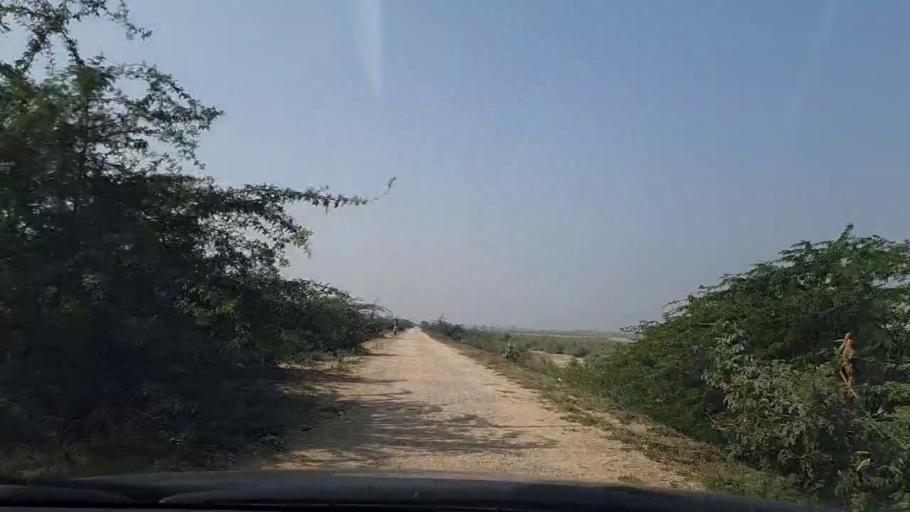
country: PK
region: Sindh
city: Mirpur Sakro
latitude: 24.5749
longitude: 67.7696
